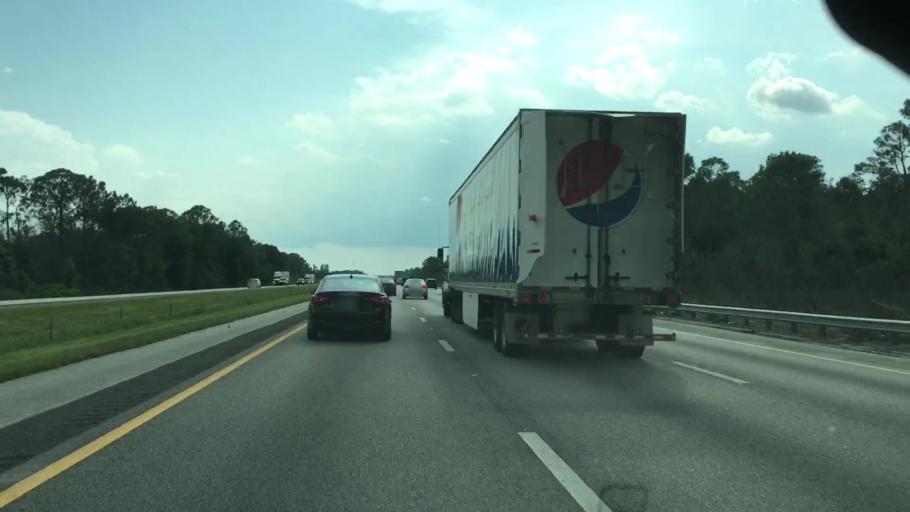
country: US
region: Florida
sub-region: Polk County
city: Davenport
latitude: 28.2080
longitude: -81.6833
